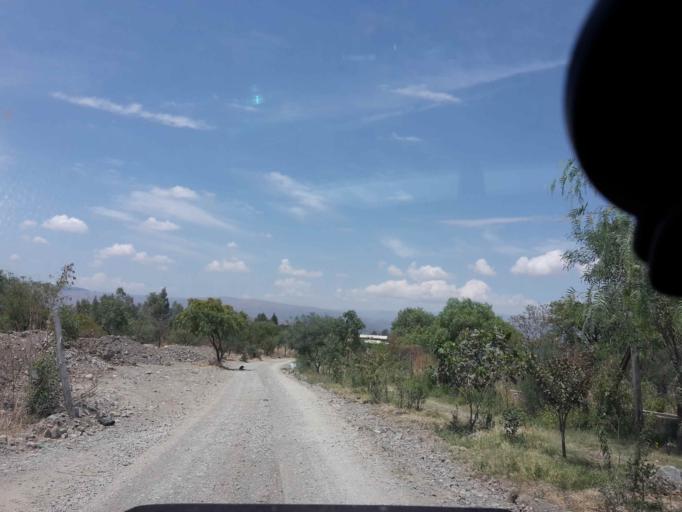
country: BO
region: Cochabamba
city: Cochabamba
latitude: -17.3329
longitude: -66.2128
